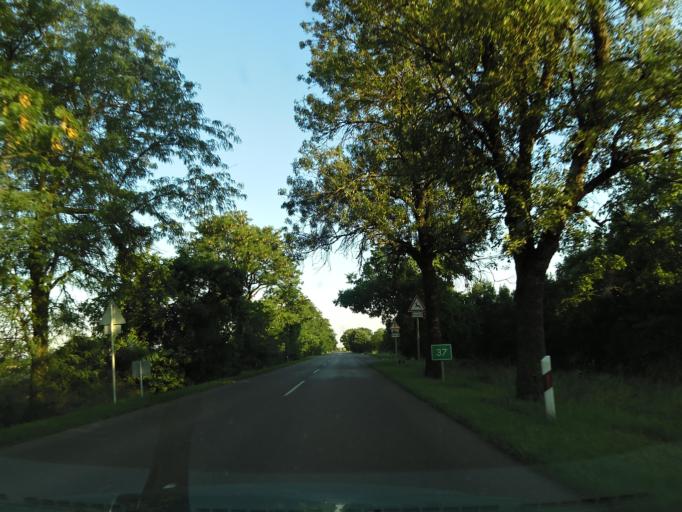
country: HU
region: Csongrad
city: Szegvar
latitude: 46.5512
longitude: 20.3166
